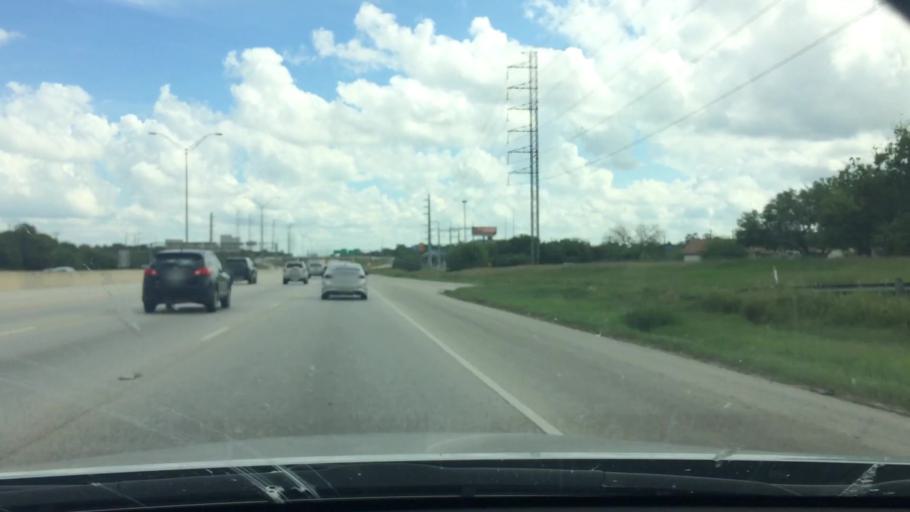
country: US
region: Texas
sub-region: Bexar County
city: San Antonio
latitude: 29.3733
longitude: -98.4574
